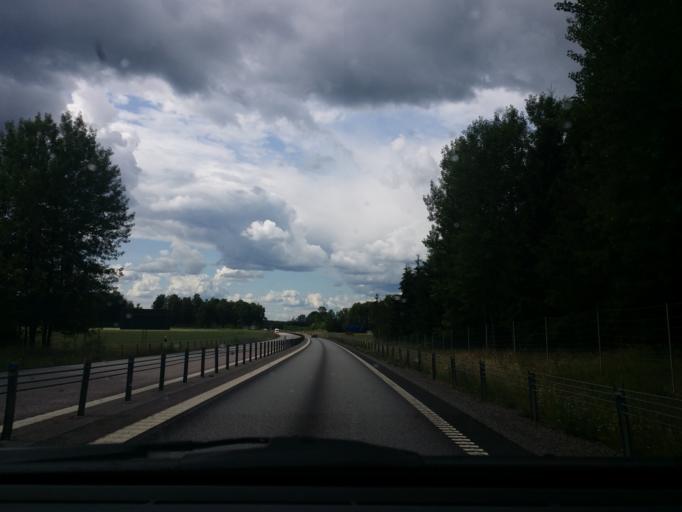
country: SE
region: Vaestmanland
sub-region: Kopings Kommun
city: Koping
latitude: 59.5731
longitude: 16.1028
